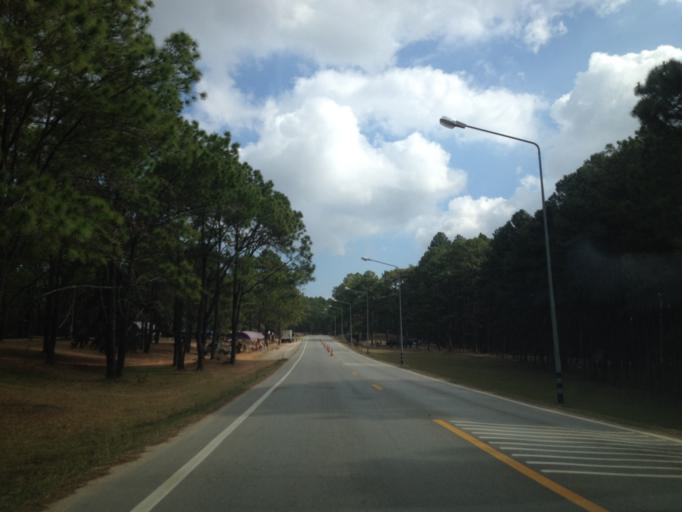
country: TH
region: Chiang Mai
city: Hot
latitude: 18.1559
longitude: 98.3869
